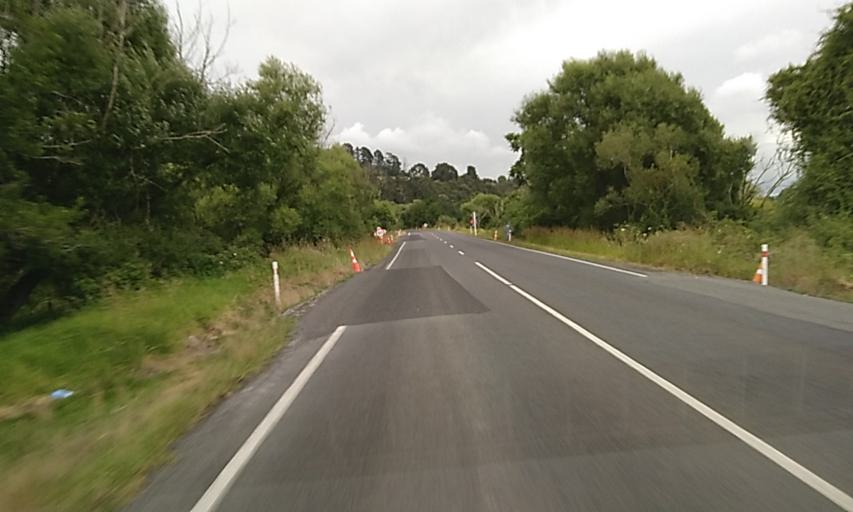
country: NZ
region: Auckland
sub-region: Auckland
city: Pukekohe East
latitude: -37.3032
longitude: 174.9494
